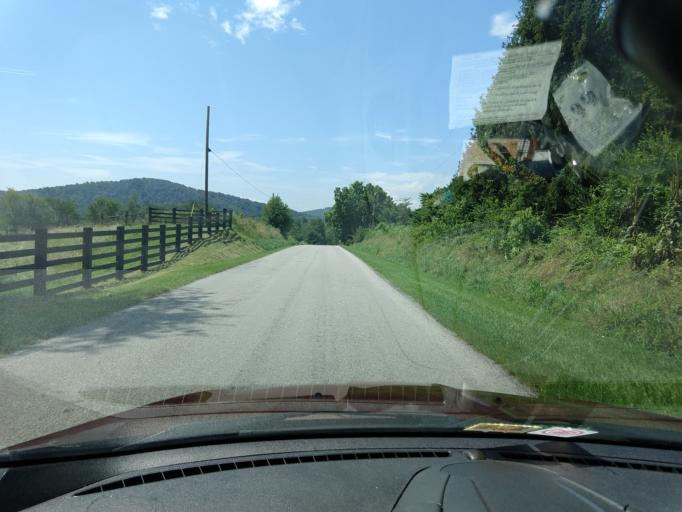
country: US
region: Virginia
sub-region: Rockingham County
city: Broadway
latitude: 38.5660
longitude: -78.8879
